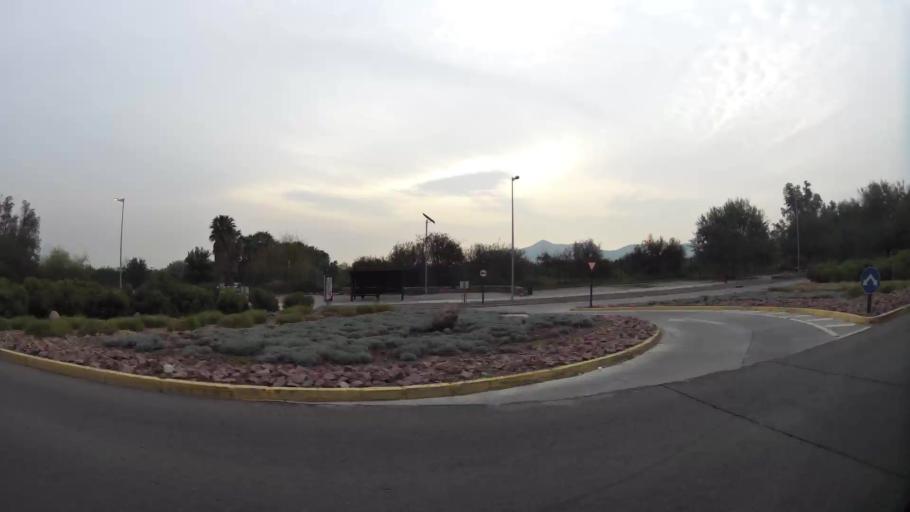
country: CL
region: Santiago Metropolitan
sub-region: Provincia de Chacabuco
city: Chicureo Abajo
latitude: -33.2690
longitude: -70.6236
